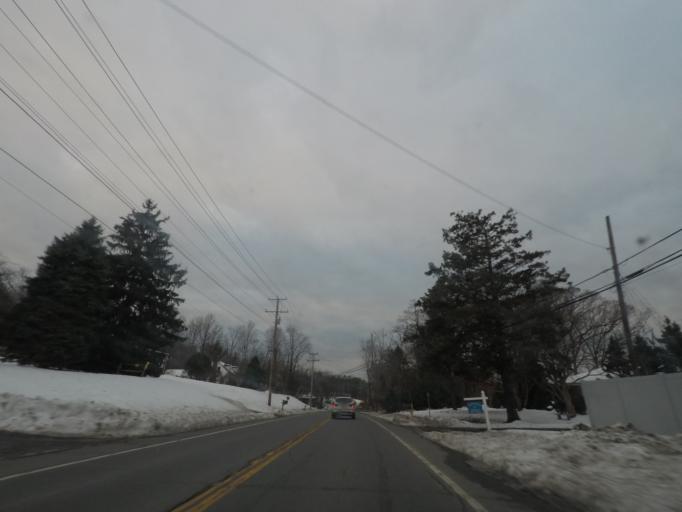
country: US
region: New York
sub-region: Orange County
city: Vails Gate
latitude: 41.4922
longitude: -74.0589
